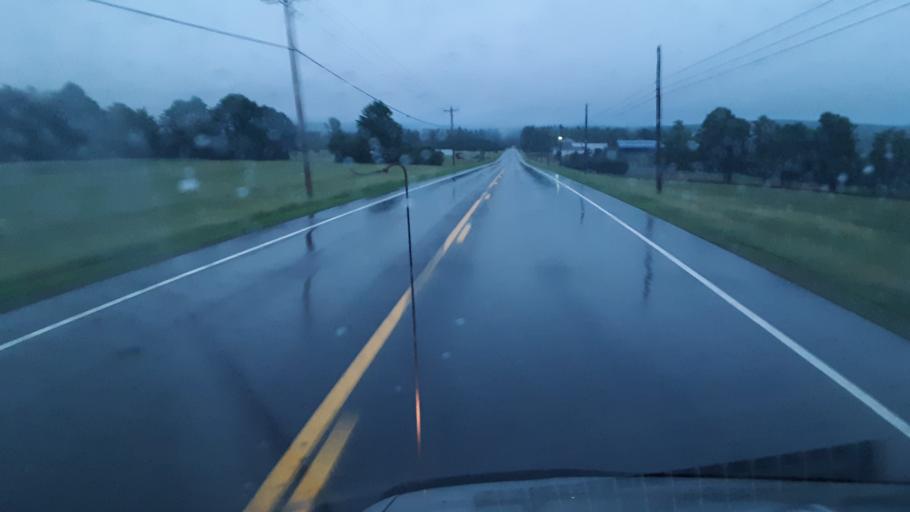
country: US
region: Maine
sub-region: Penobscot County
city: Patten
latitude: 45.9537
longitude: -68.4524
